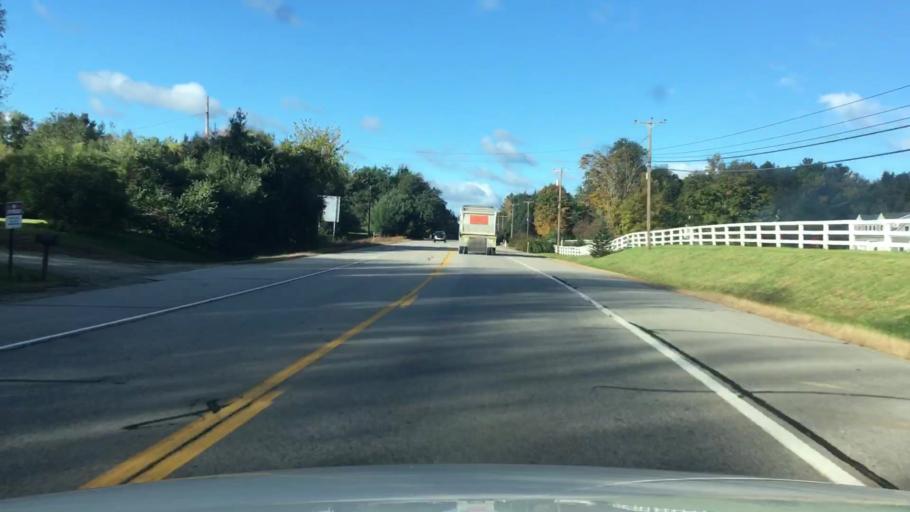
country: US
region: New Hampshire
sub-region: Strafford County
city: Lee
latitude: 43.1506
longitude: -70.9838
